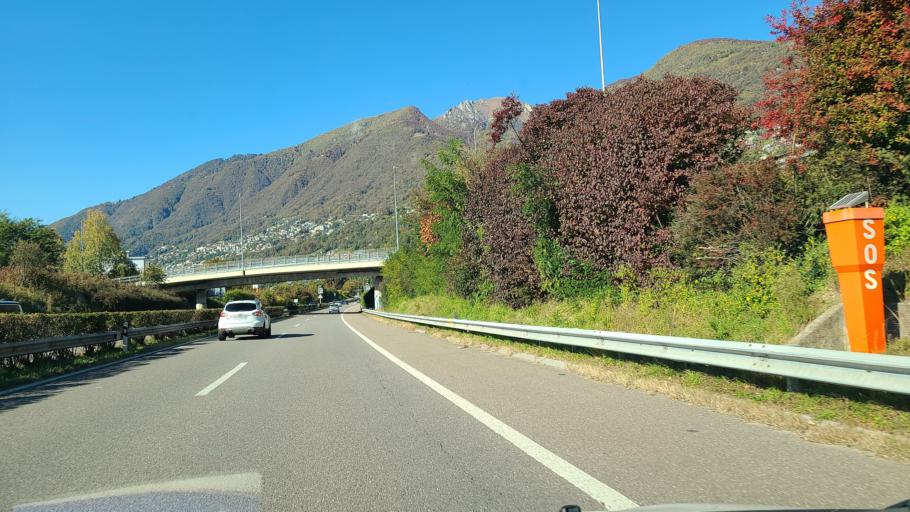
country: CH
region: Ticino
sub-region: Locarno District
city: Gordola
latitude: 46.1754
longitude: 8.8506
